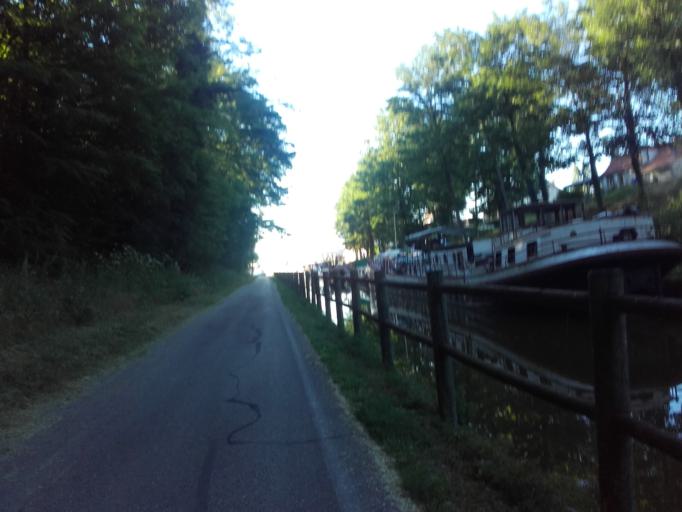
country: FR
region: Bourgogne
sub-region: Departement de Saone-et-Loire
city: Chagny
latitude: 46.9007
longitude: 4.7538
